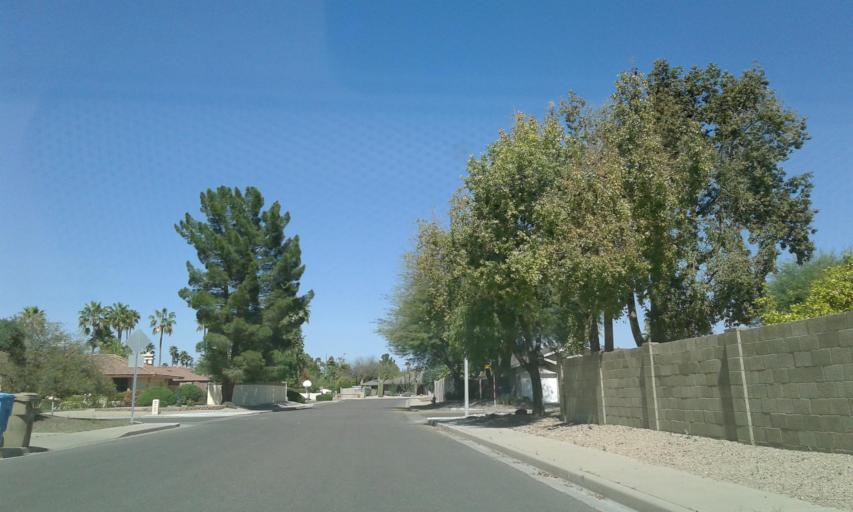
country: US
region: Arizona
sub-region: Maricopa County
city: Paradise Valley
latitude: 33.5935
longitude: -111.9649
